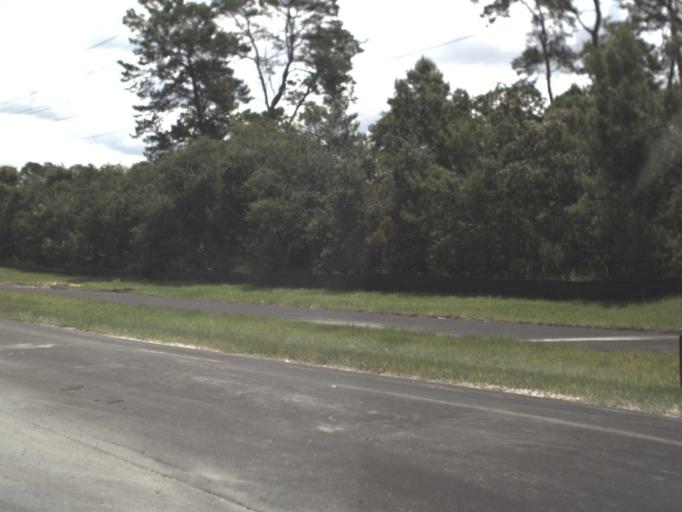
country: US
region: Florida
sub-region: Hernando County
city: North Weeki Wachee
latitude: 28.5194
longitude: -82.5674
